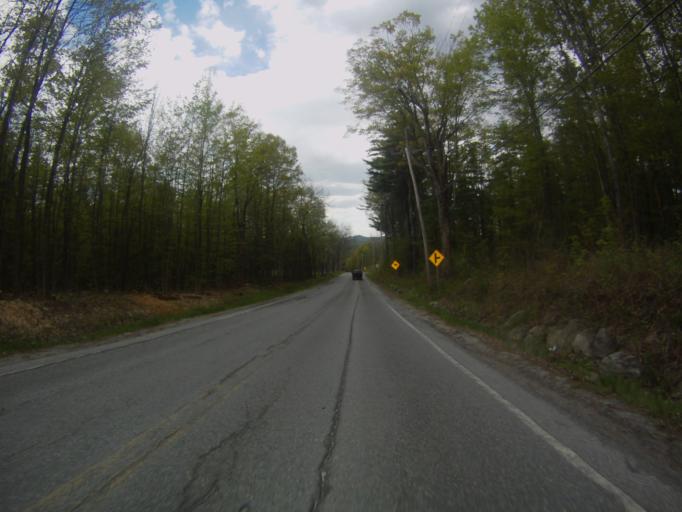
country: US
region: New York
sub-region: Essex County
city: Mineville
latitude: 44.0789
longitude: -73.5280
